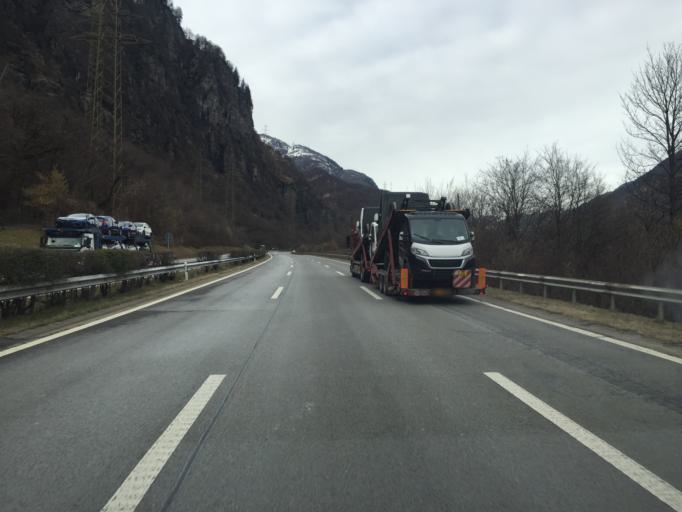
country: CH
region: Ticino
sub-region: Leventina District
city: Bodio
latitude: 46.3976
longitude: 8.8727
